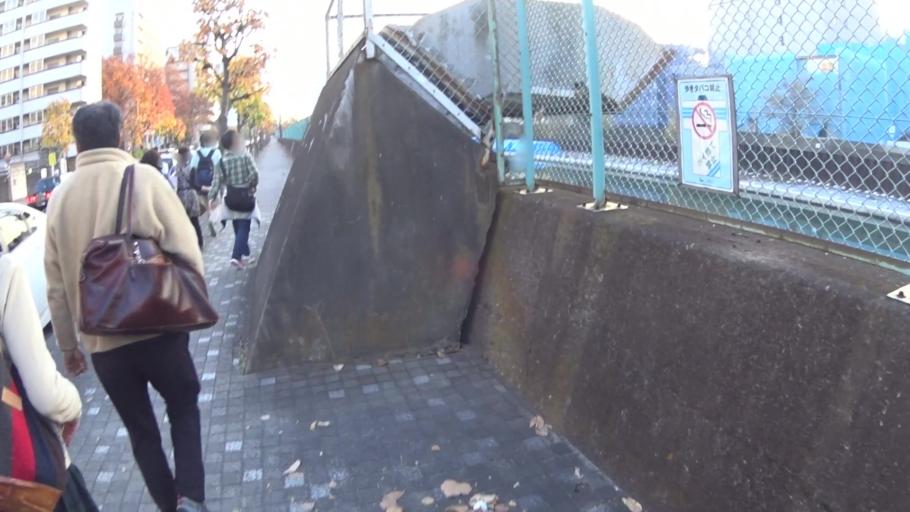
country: JP
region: Tokyo
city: Urayasu
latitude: 35.7003
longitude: 139.8191
